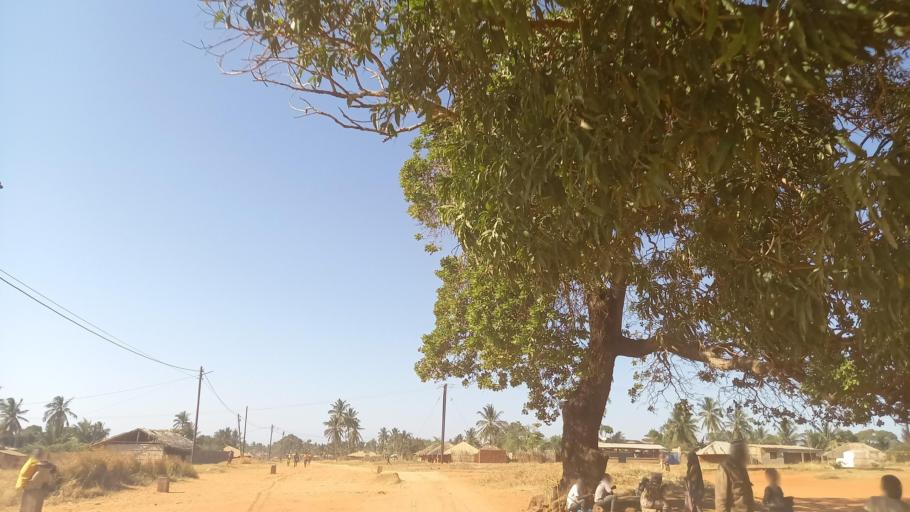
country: MZ
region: Cabo Delgado
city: Pemba
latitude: -13.1350
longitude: 40.5489
